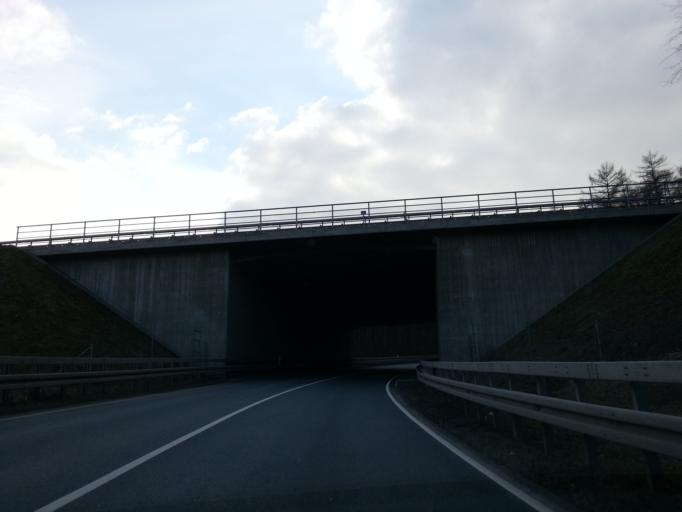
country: DE
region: Bavaria
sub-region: Regierungsbezirk Unterfranken
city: Waldbrunn
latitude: 49.7679
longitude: 9.7754
